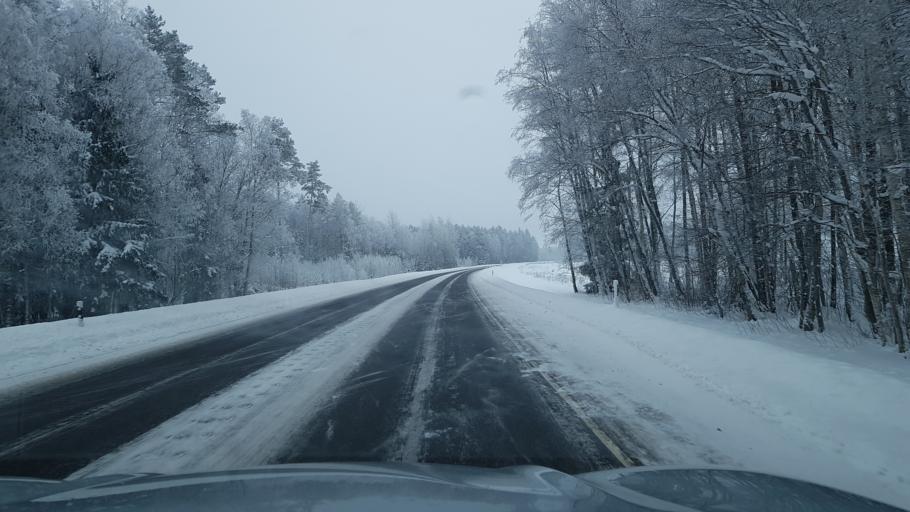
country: EE
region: Ida-Virumaa
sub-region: Johvi vald
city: Johvi
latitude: 59.2945
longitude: 27.3987
